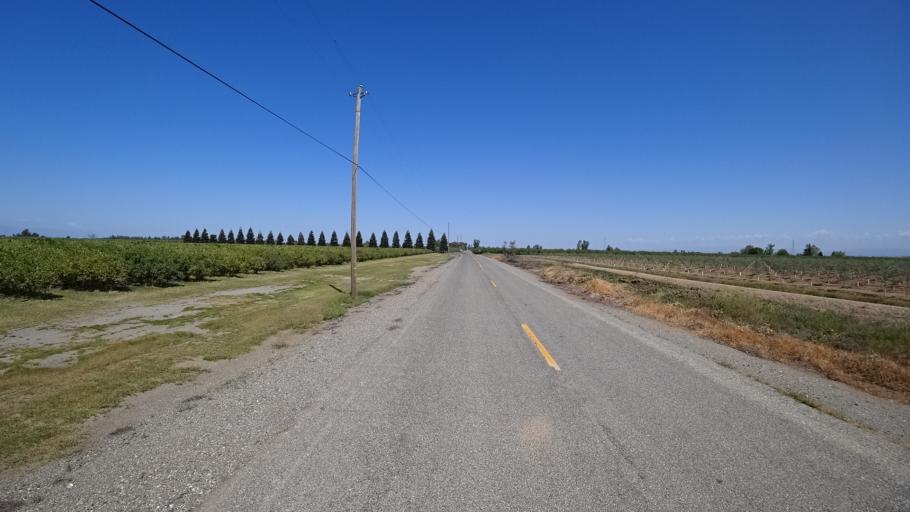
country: US
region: California
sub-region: Glenn County
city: Orland
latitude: 39.7852
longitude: -122.1690
